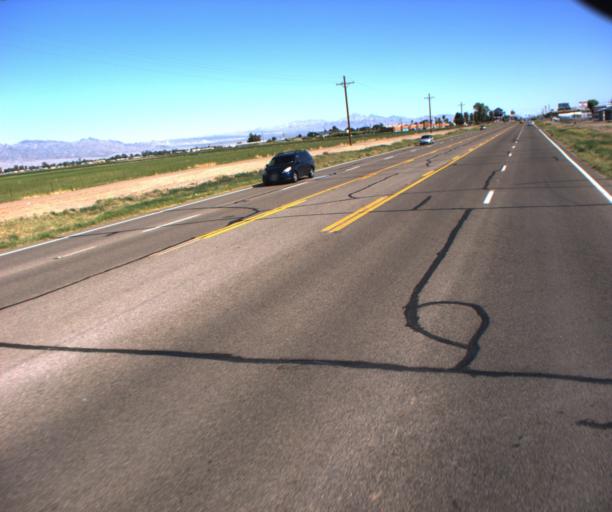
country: US
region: Arizona
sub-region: Mohave County
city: Willow Valley
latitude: 34.9024
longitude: -114.5978
